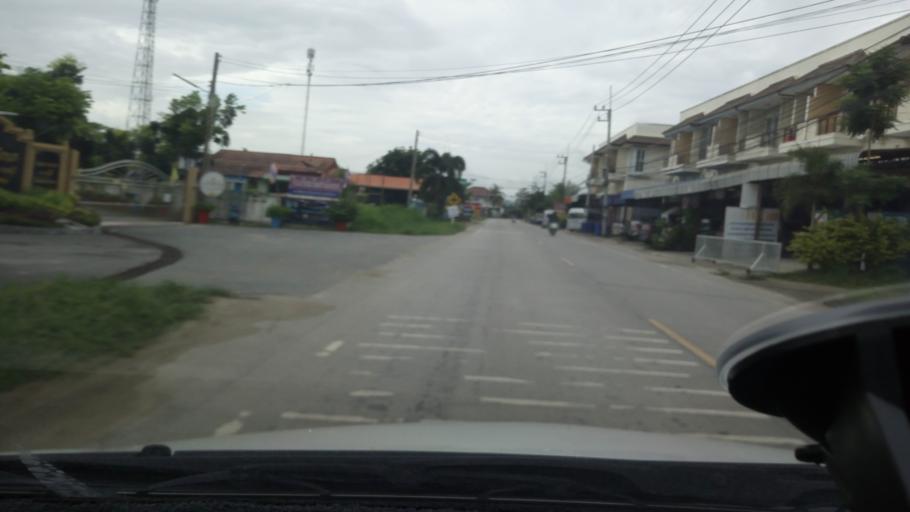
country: TH
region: Chon Buri
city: Ban Bueng
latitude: 13.3645
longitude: 101.0593
